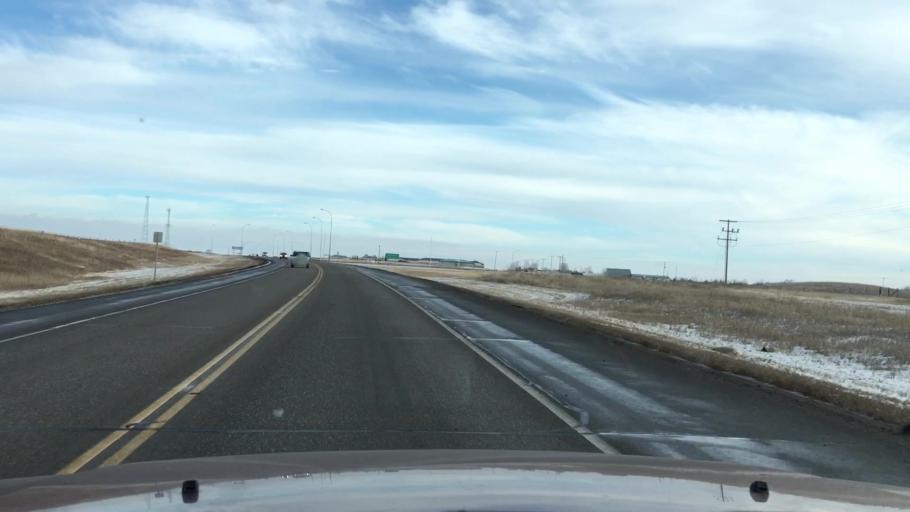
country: CA
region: Saskatchewan
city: Pilot Butte
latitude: 50.4845
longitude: -104.4403
